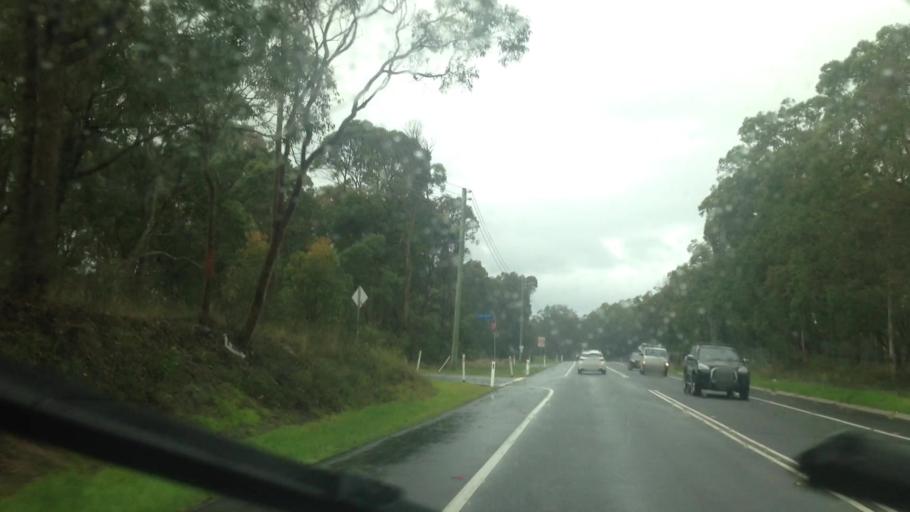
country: AU
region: New South Wales
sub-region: Lake Macquarie Shire
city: Dora Creek
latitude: -33.1223
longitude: 151.4763
